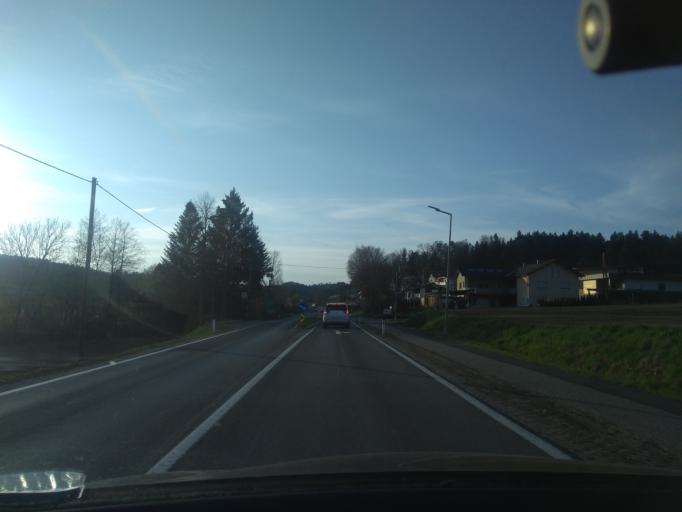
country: AT
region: Styria
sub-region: Politischer Bezirk Leibnitz
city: Heiligenkreuz am Waasen
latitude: 46.9749
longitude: 15.5807
